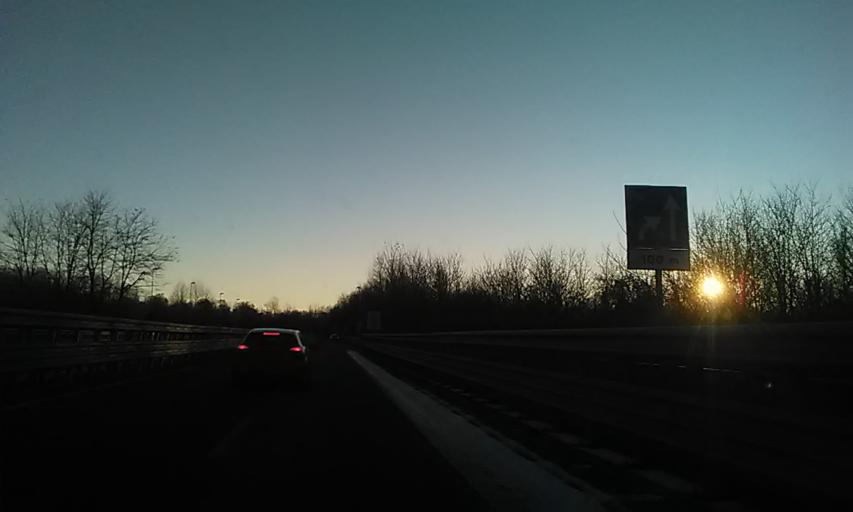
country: IT
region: Piedmont
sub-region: Provincia di Biella
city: Castelletto Cervo
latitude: 45.5518
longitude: 8.2357
